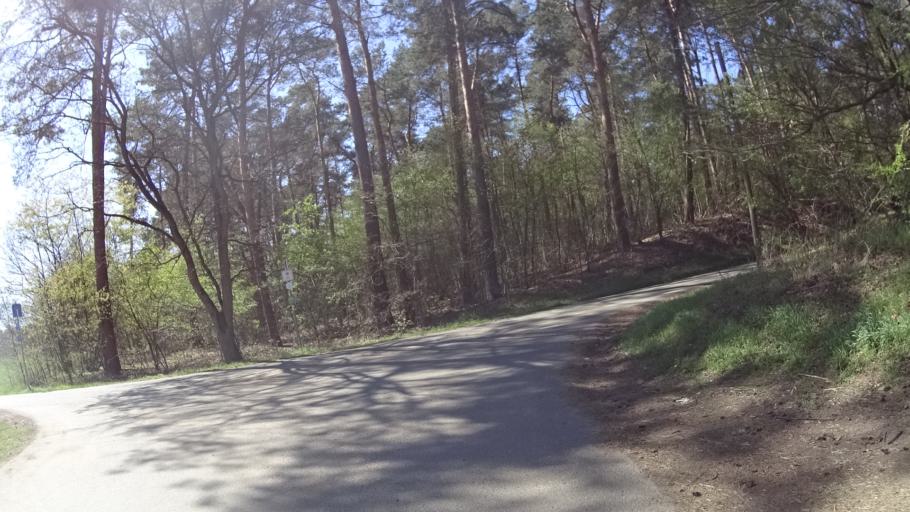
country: DE
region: North Rhine-Westphalia
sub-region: Regierungsbezirk Munster
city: Dulmen
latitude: 51.7842
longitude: 7.2661
